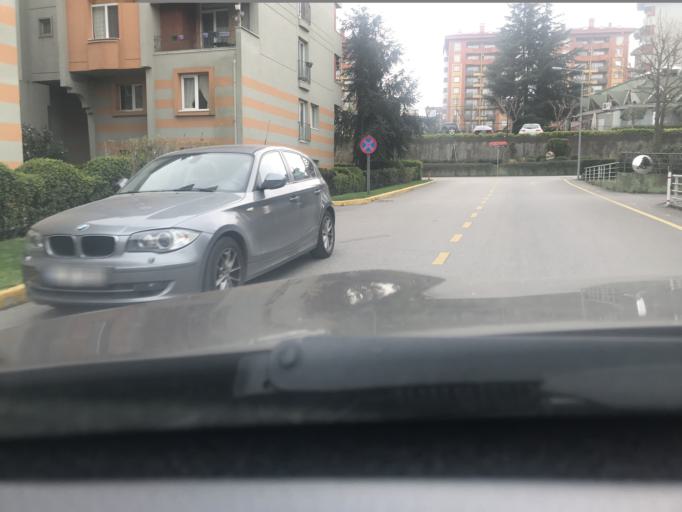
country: TR
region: Istanbul
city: Umraniye
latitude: 41.0320
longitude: 29.1573
